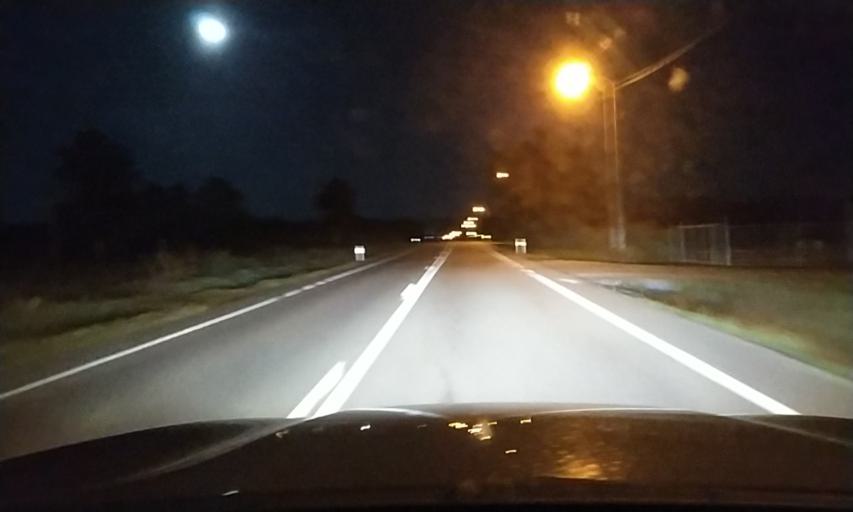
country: ES
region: Galicia
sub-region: Provincia de Ourense
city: Verin
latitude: 41.9460
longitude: -7.4843
